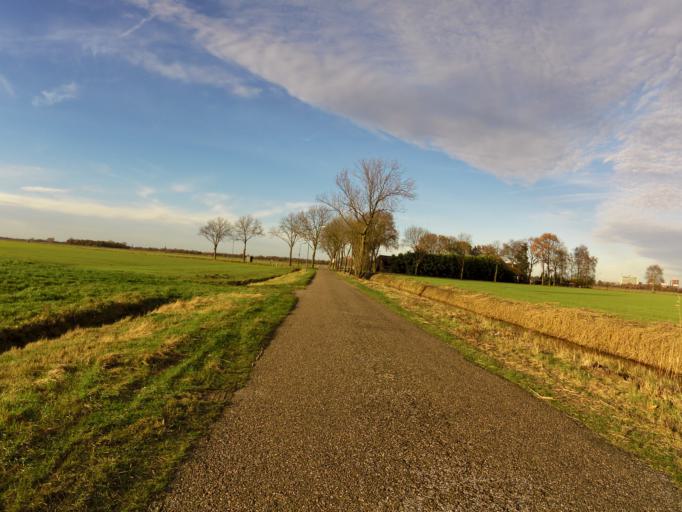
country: NL
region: North Brabant
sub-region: Gemeente Vught
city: Vught
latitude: 51.6705
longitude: 5.2714
